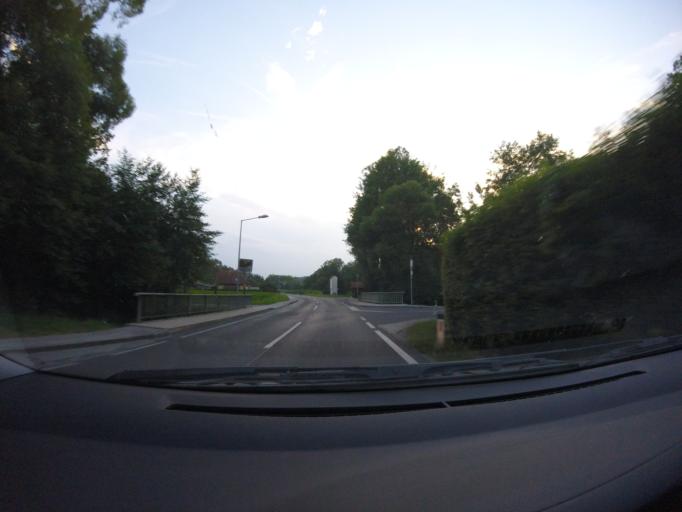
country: AT
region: Styria
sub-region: Politischer Bezirk Graz-Umgebung
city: Edelsgrub
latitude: 47.0640
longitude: 15.5629
